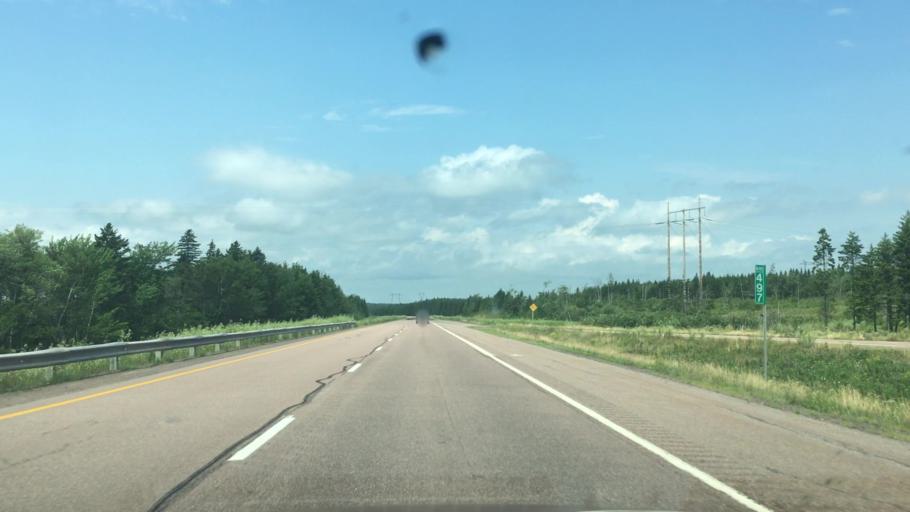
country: CA
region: New Brunswick
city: Sackville
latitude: 45.9613
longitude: -64.4179
